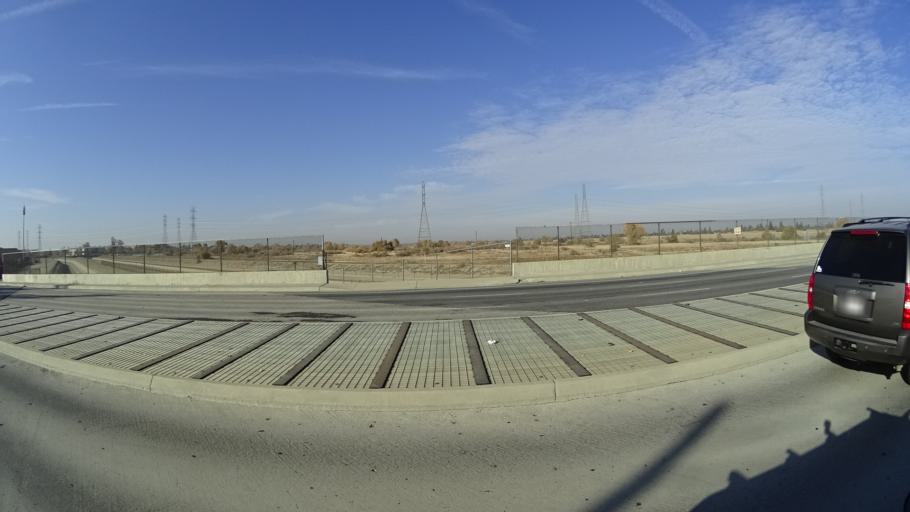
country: US
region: California
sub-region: Kern County
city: Greenacres
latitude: 35.3592
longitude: -119.0921
